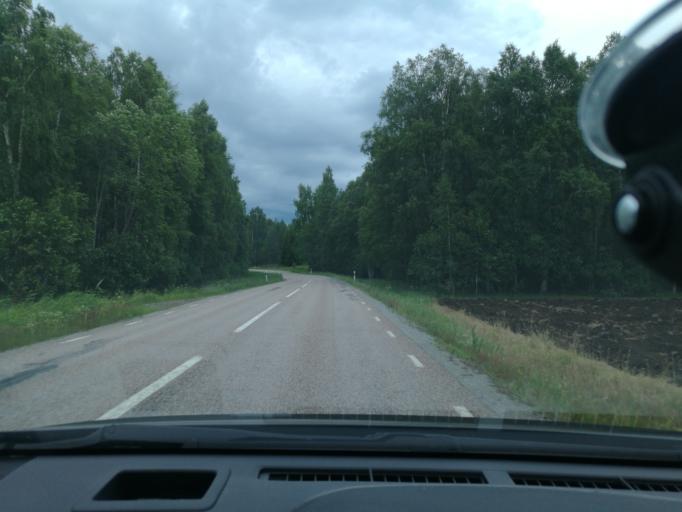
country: SE
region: Vaestmanland
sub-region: Sala Kommun
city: Sala
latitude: 59.9155
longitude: 16.4452
